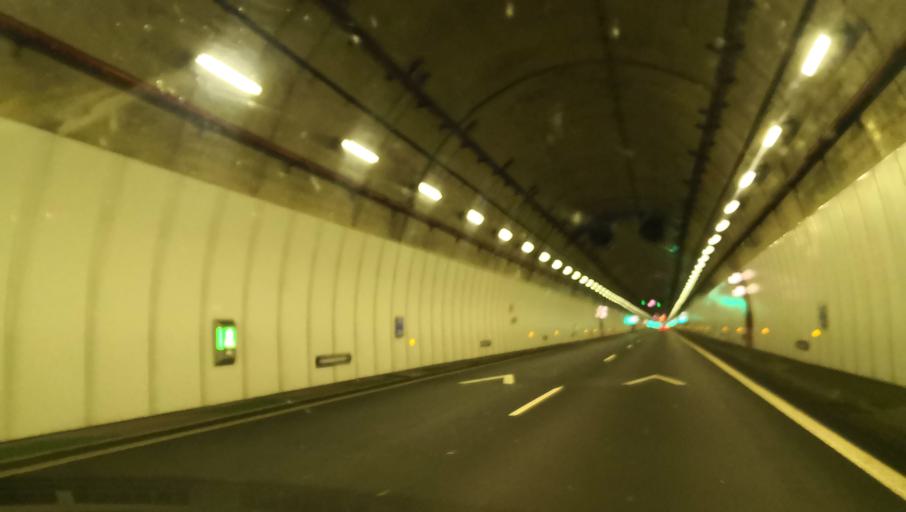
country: ES
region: Galicia
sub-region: Provincia de Pontevedra
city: Covelo
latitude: 42.1786
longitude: -8.3455
